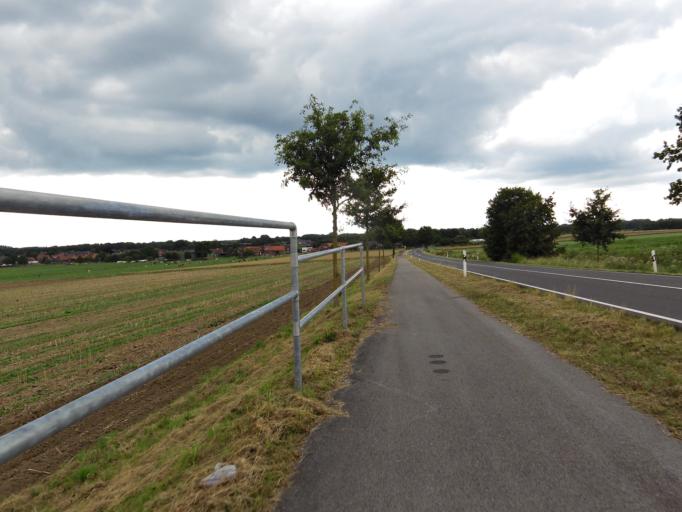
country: DE
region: North Rhine-Westphalia
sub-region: Regierungsbezirk Koln
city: Selfkant
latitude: 51.0148
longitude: 5.9353
